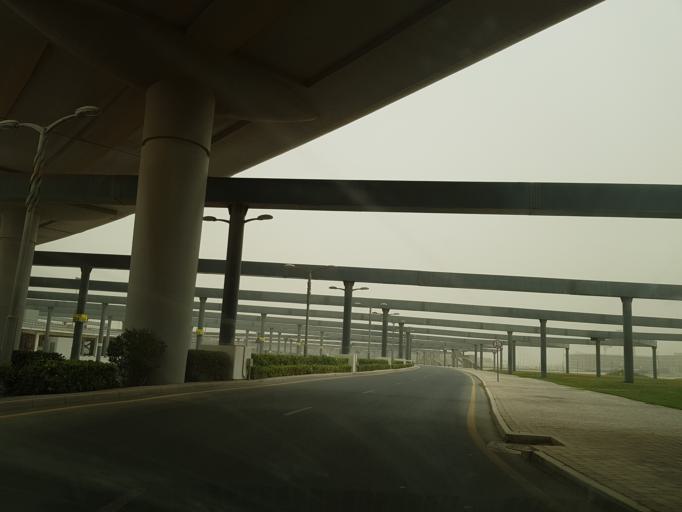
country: AE
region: Dubai
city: Dubai
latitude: 25.1592
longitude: 55.2980
